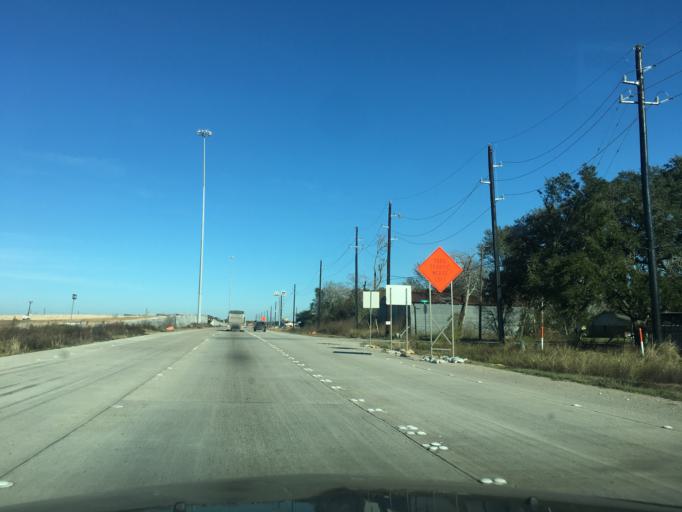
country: US
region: Texas
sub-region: Fort Bend County
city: Rosenberg
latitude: 29.5301
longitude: -95.8634
